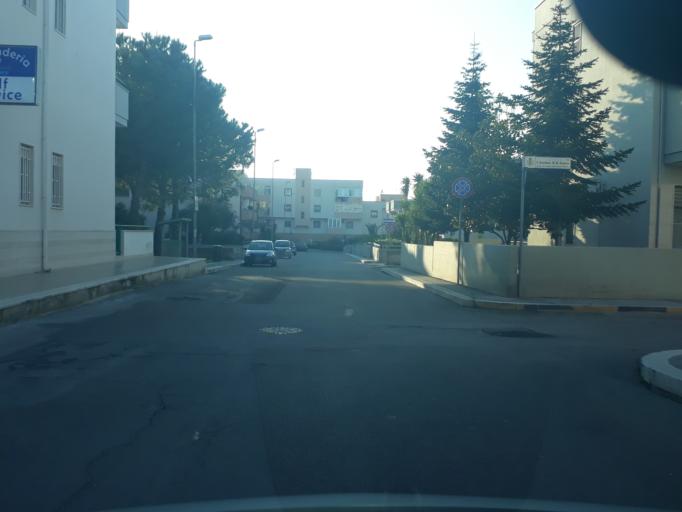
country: IT
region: Apulia
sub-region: Provincia di Bari
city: Locorotondo
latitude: 40.7583
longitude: 17.3315
